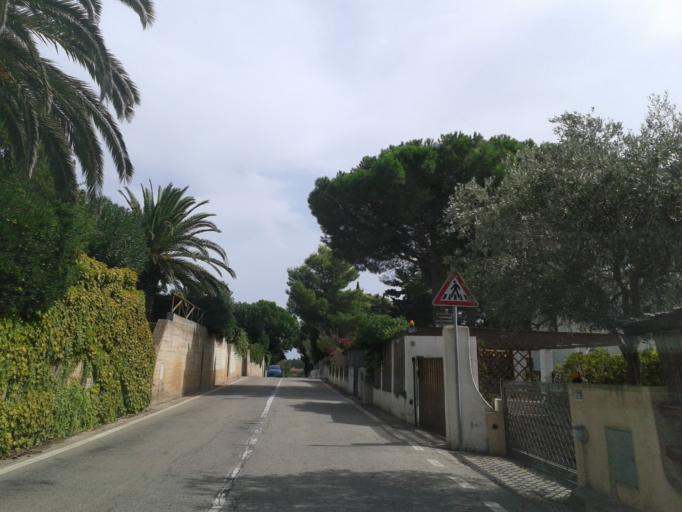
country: IT
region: Sardinia
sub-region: Provincia di Cagliari
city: Villasimius
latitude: 39.1317
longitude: 9.5061
